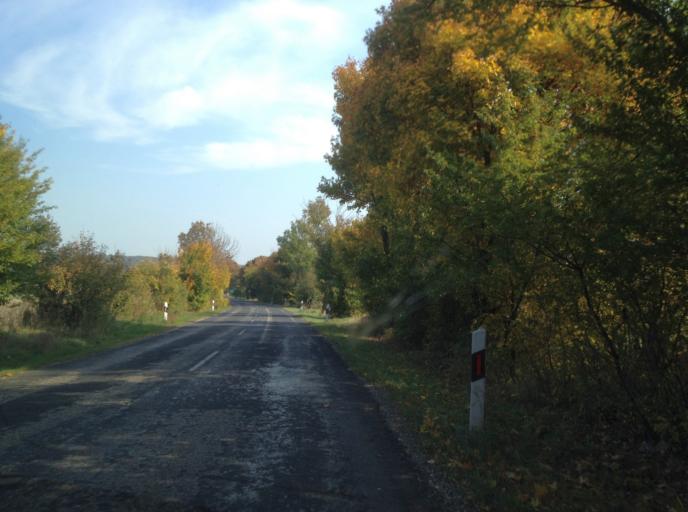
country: HU
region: Komarom-Esztergom
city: Tardos
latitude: 47.6410
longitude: 18.4519
